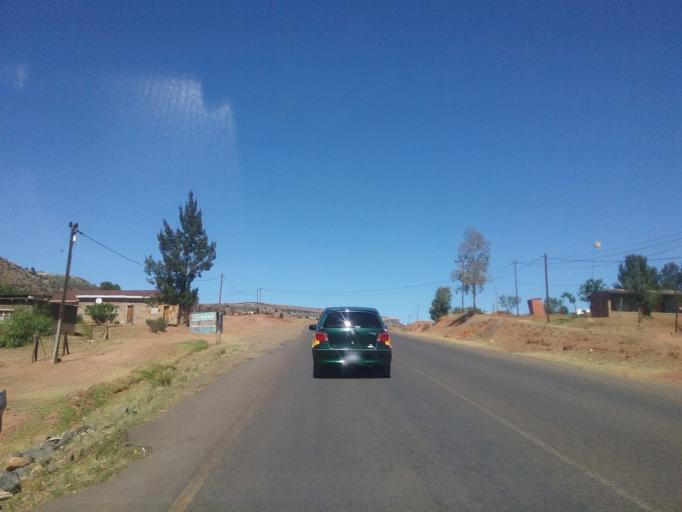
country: LS
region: Quthing
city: Quthing
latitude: -30.3978
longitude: 27.6602
